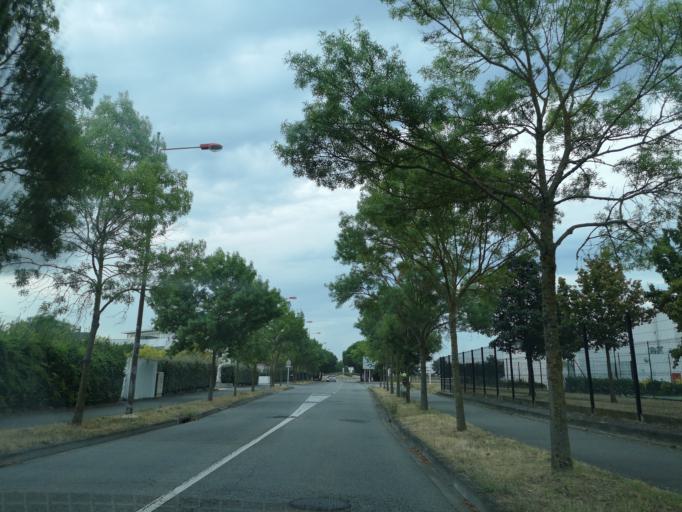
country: FR
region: Midi-Pyrenees
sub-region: Departement de la Haute-Garonne
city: Cugnaux
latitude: 43.5799
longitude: 1.3777
